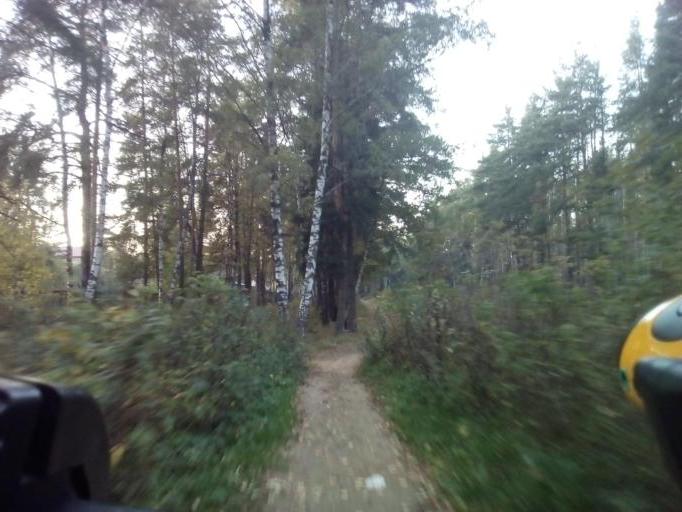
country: RU
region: Moskovskaya
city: Ramenskoye
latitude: 55.5939
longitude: 38.2154
